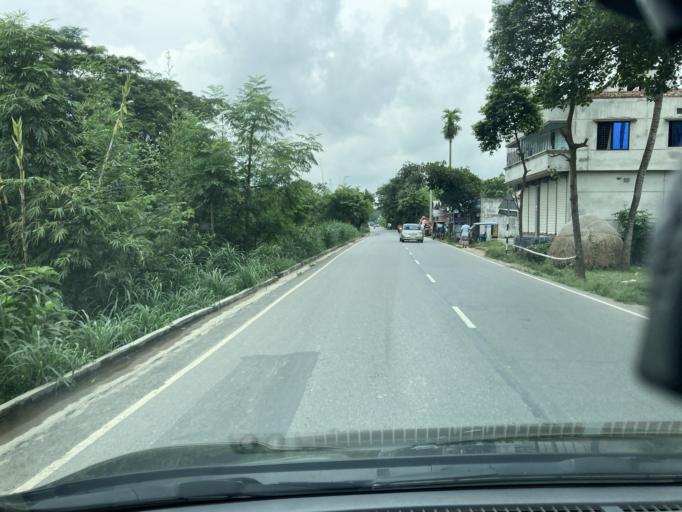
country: BD
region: Dhaka
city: Azimpur
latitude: 23.8061
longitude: 90.2066
